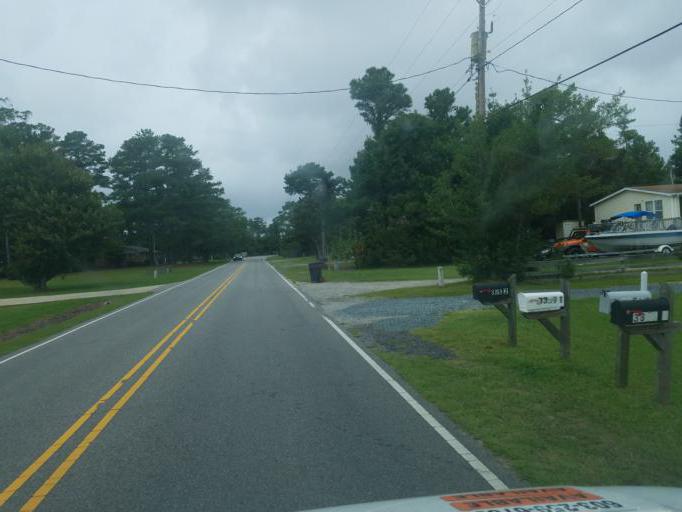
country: US
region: North Carolina
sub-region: Dare County
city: Wanchese
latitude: 35.8478
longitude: -75.6398
